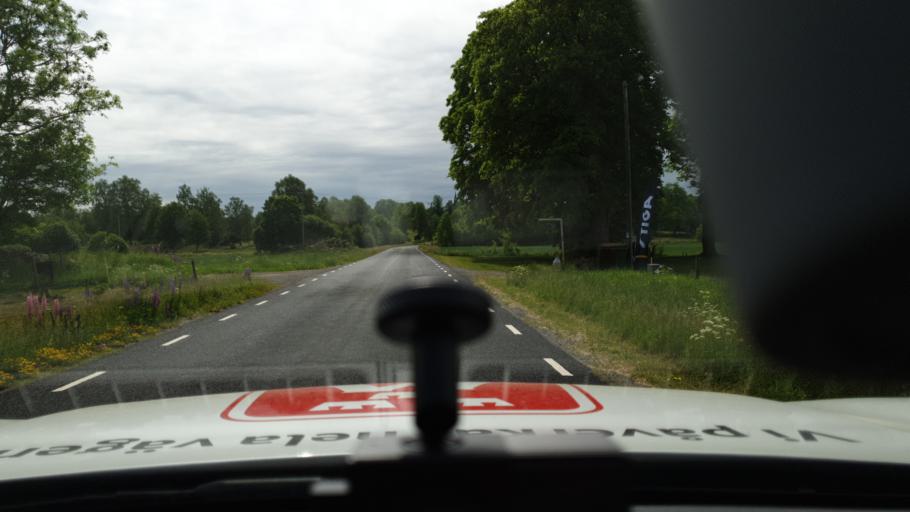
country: SE
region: Vaestra Goetaland
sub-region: Falkopings Kommun
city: Falkoeping
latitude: 58.0184
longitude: 13.6920
